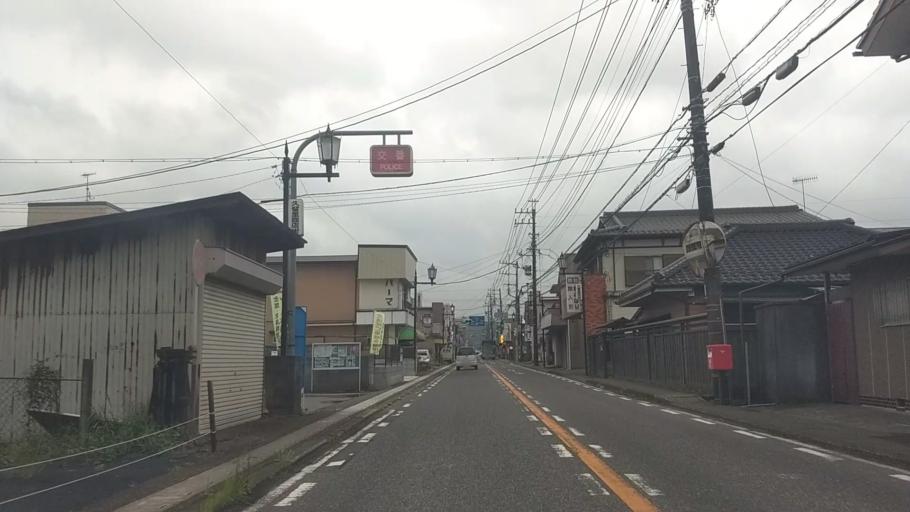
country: JP
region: Chiba
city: Kisarazu
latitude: 35.2971
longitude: 140.0763
